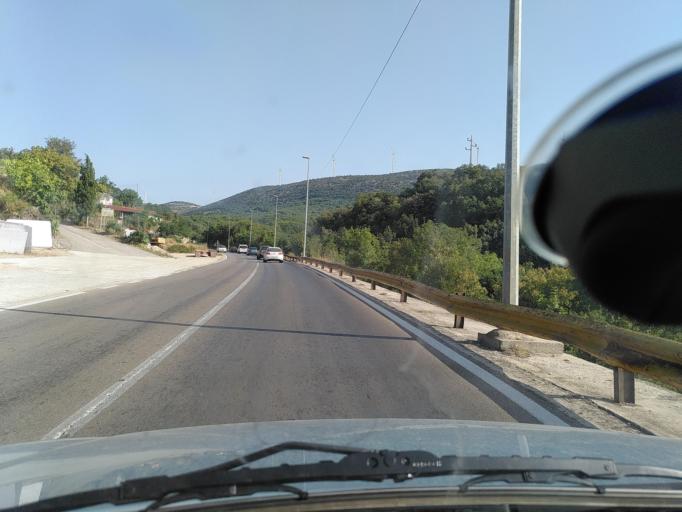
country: ME
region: Ulcinj
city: Ulcinj
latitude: 41.9635
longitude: 19.1913
